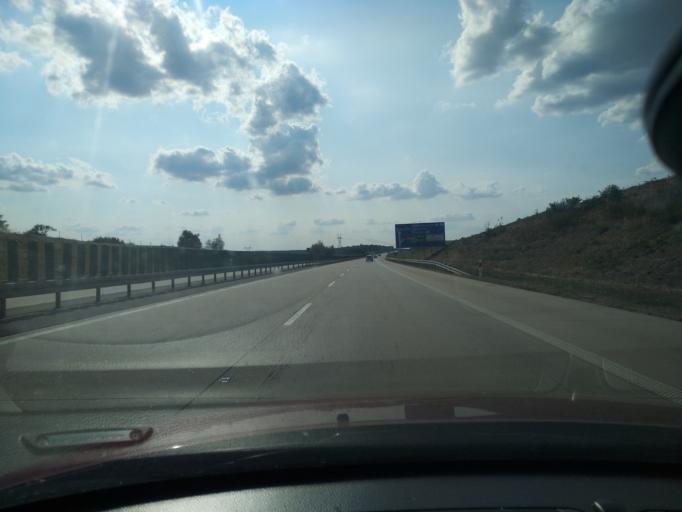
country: PL
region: Lower Silesian Voivodeship
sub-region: Powiat zgorzelecki
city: Wegliniec
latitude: 51.2173
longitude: 15.2587
